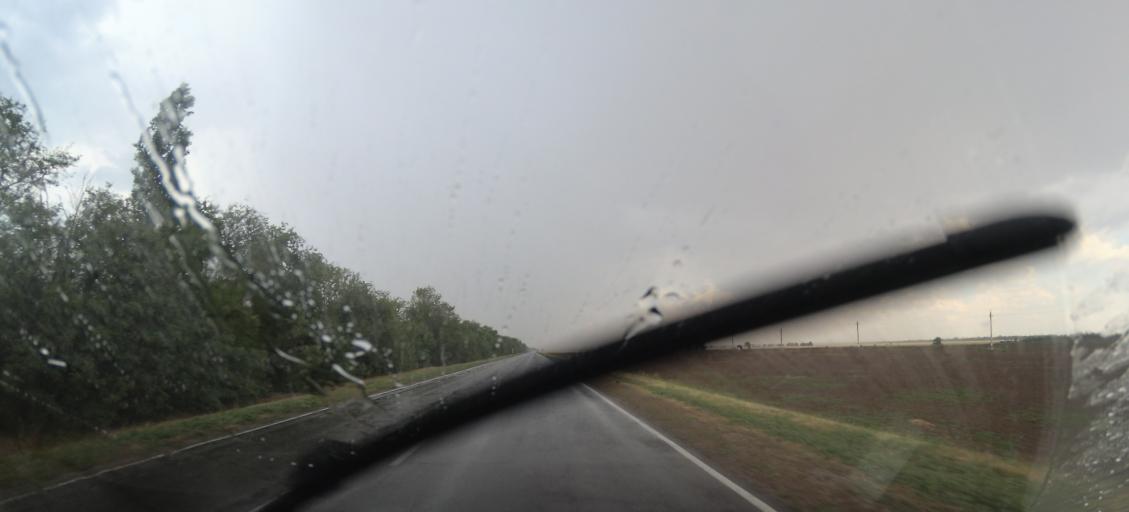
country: RU
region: Rostov
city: Proletarsk
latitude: 46.6585
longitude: 41.6836
